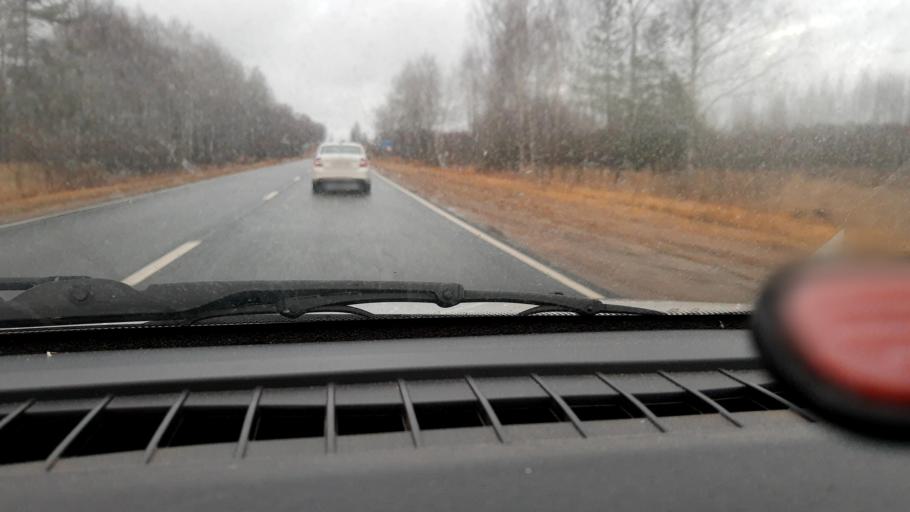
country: RU
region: Nizjnij Novgorod
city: Krasnyye Baki
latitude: 57.0912
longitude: 45.1489
